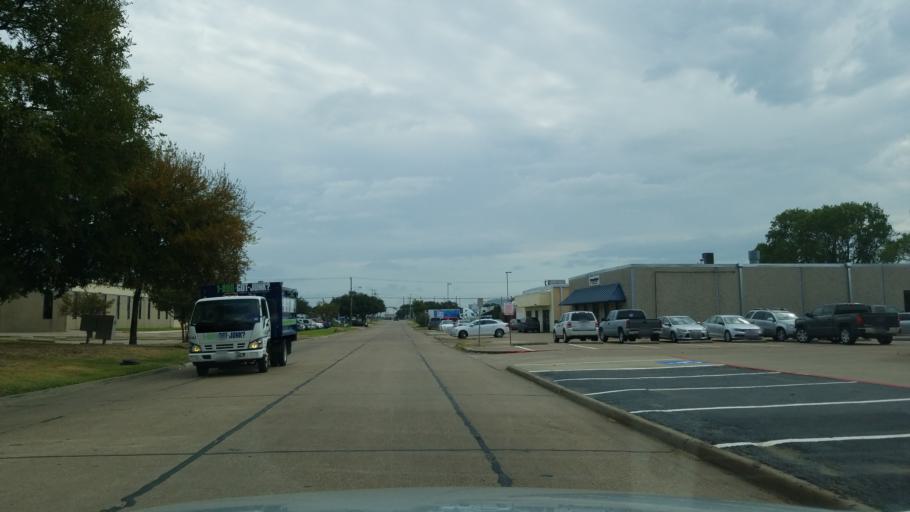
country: US
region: Texas
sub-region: Dallas County
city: Garland
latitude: 32.9017
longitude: -96.6867
